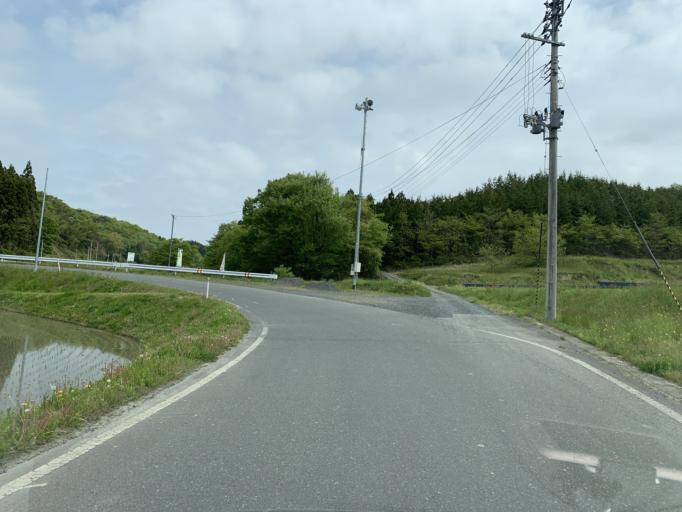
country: JP
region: Iwate
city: Ichinoseki
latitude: 38.8529
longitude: 141.1974
